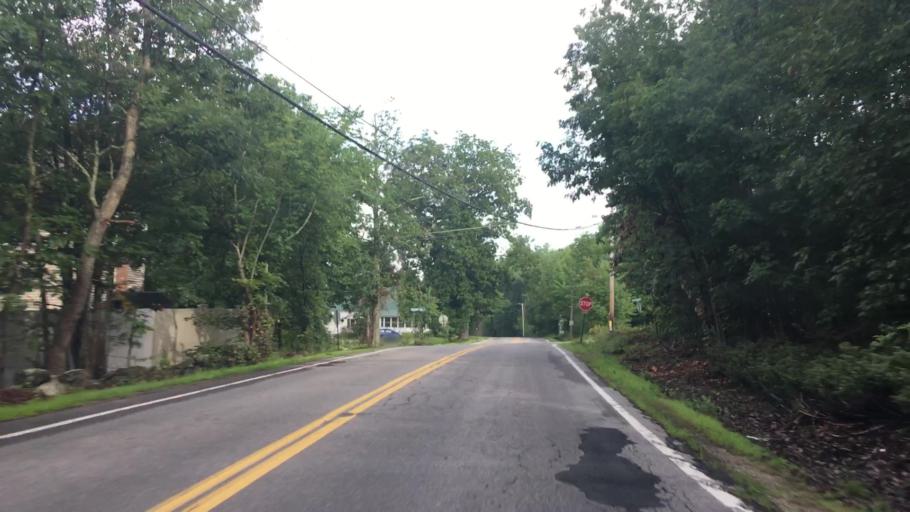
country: US
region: New Hampshire
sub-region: Strafford County
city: Rochester
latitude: 43.3593
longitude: -70.9951
